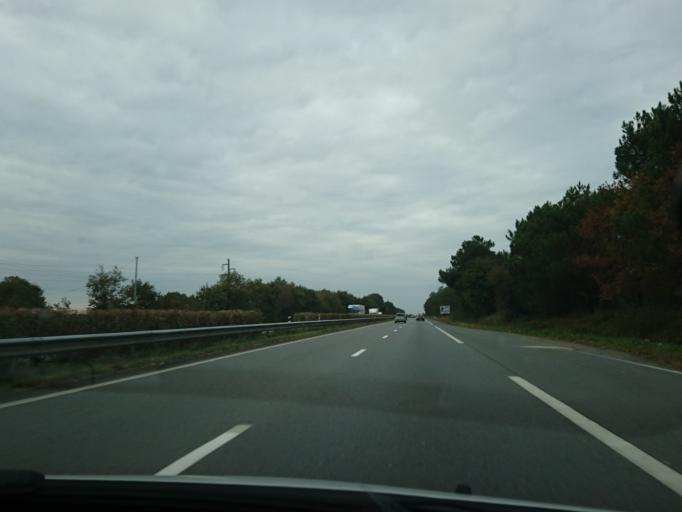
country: FR
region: Pays de la Loire
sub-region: Departement de la Loire-Atlantique
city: La Chapelle-des-Marais
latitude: 47.4909
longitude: -2.2355
